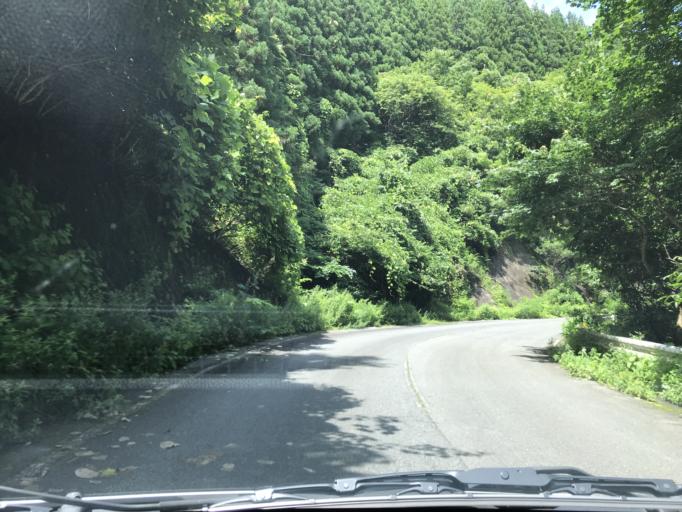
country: JP
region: Iwate
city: Tono
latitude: 39.0791
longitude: 141.4095
